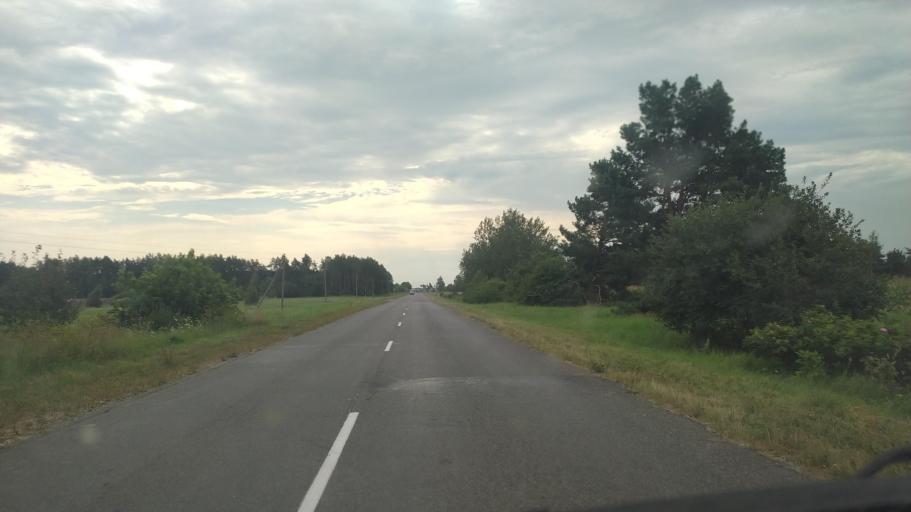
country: BY
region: Brest
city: Byaroza
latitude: 52.5614
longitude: 24.9079
